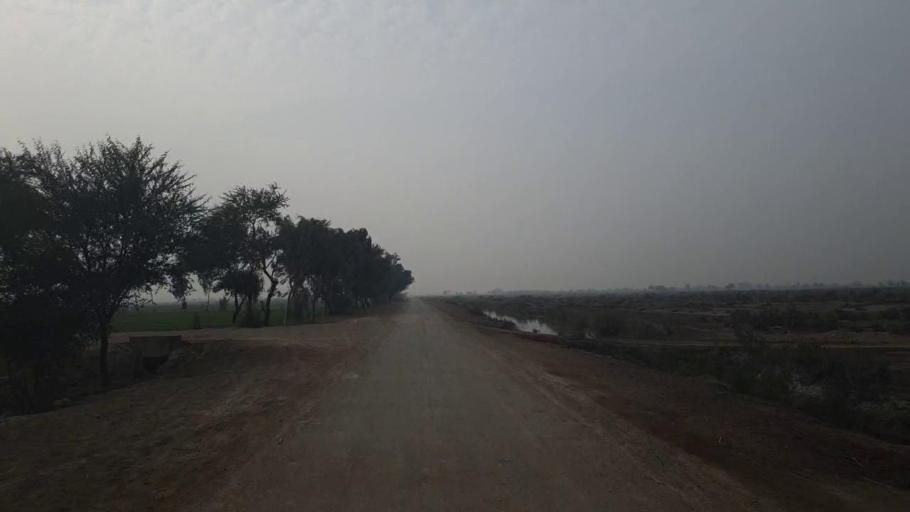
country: PK
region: Sindh
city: Tando Adam
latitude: 25.8231
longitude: 68.6959
